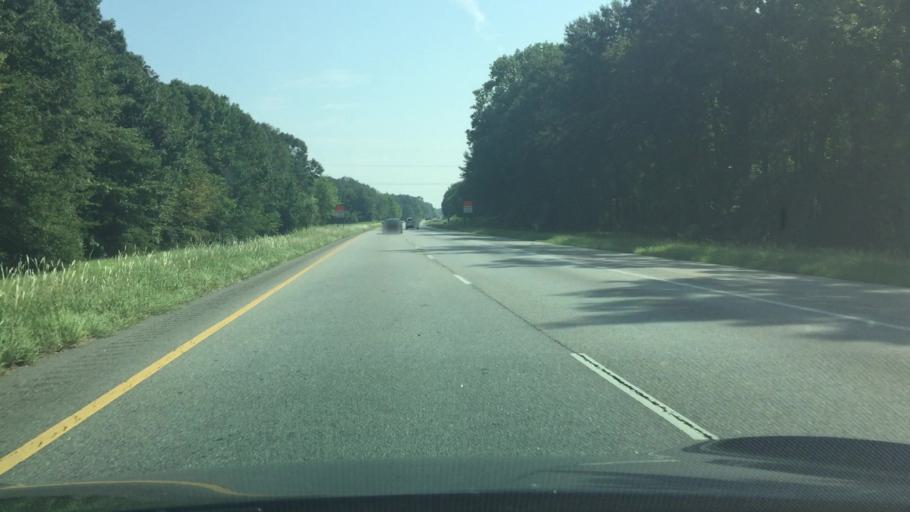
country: US
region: Alabama
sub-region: Lowndes County
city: Hayneville
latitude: 32.2113
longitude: -86.4061
